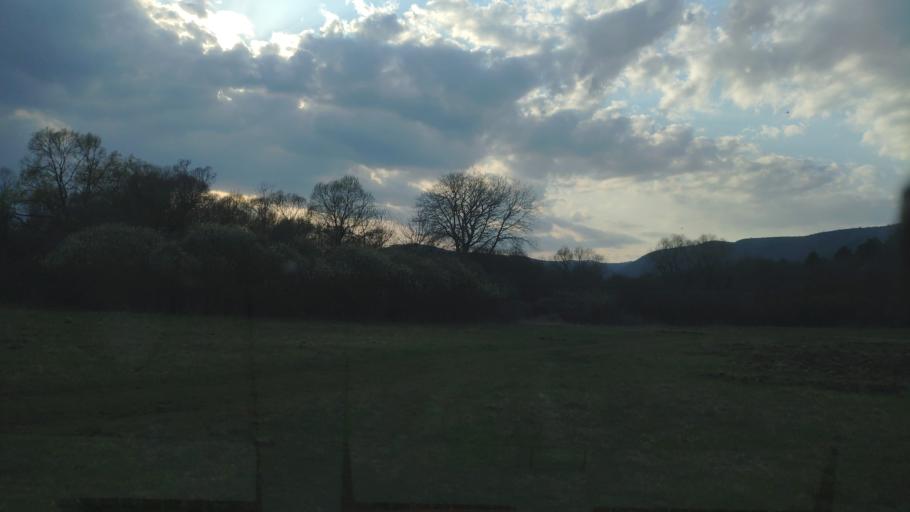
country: SK
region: Kosicky
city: Moldava nad Bodvou
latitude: 48.6160
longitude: 20.9170
